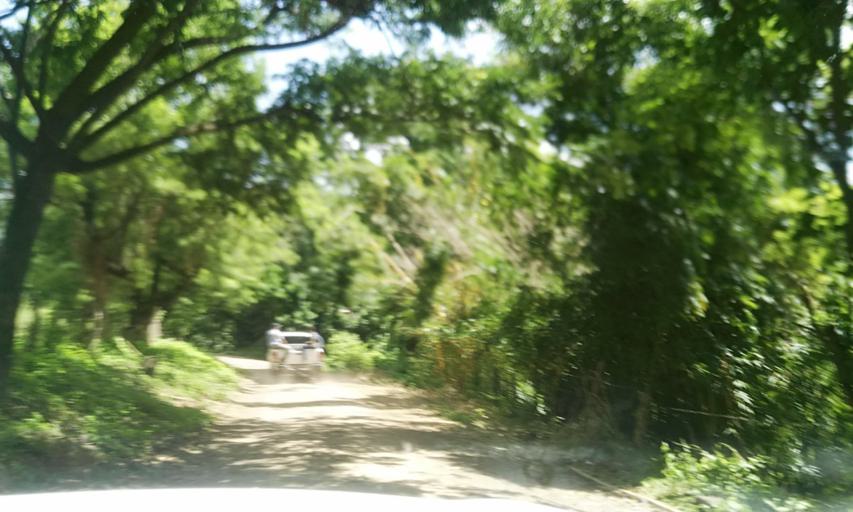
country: NI
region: Matagalpa
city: Terrabona
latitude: 12.7174
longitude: -85.9240
